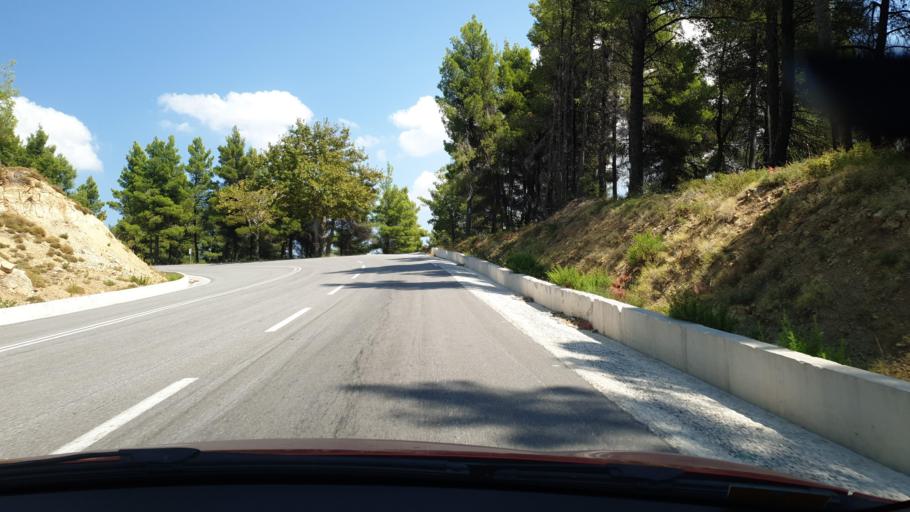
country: GR
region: Central Greece
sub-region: Nomos Evvoias
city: Politika
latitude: 38.6451
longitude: 23.5637
